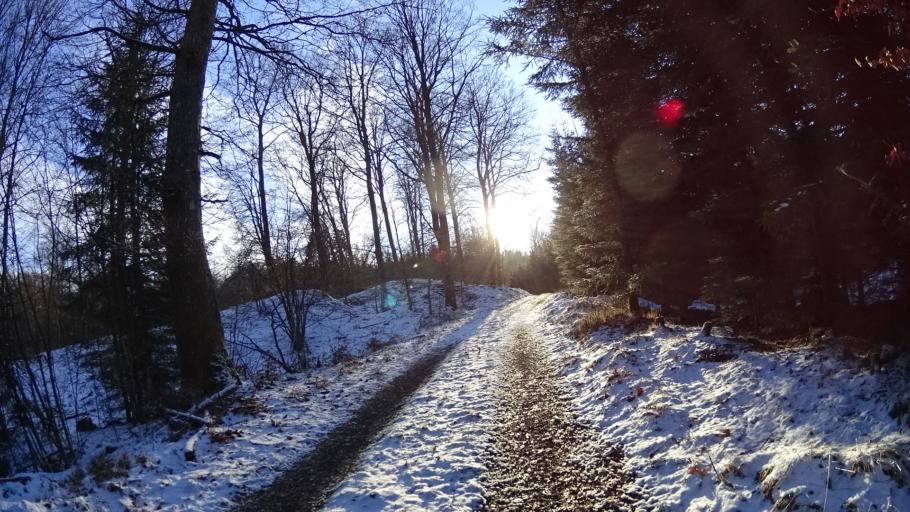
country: SE
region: Skane
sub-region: Hoors Kommun
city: Hoeoer
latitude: 55.9935
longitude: 13.5553
